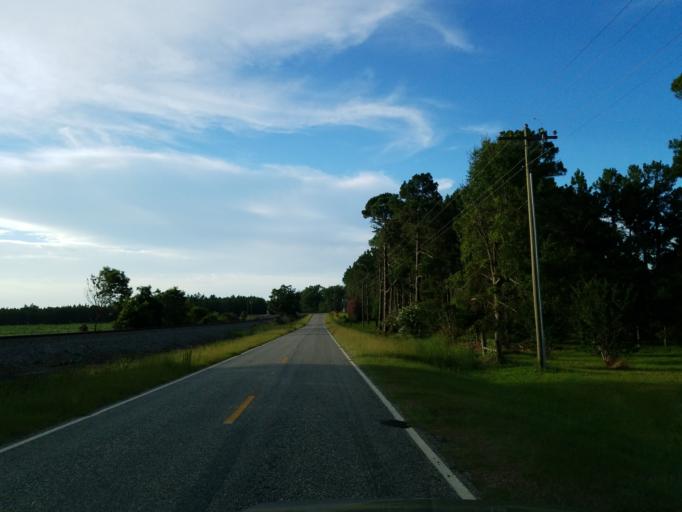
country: US
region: Georgia
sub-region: Tift County
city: Tifton
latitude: 31.5667
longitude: -83.5669
